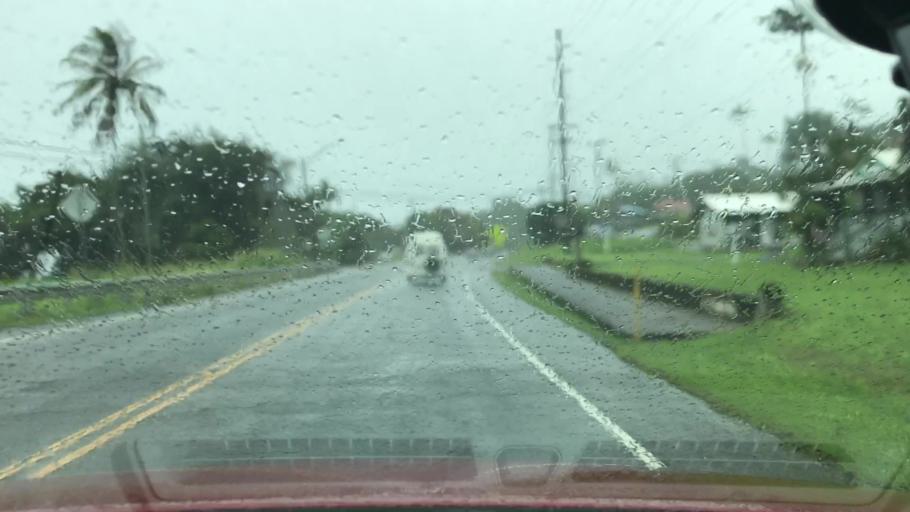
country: US
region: Hawaii
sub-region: Hawaii County
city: Pepeekeo
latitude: 19.9847
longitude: -155.2341
